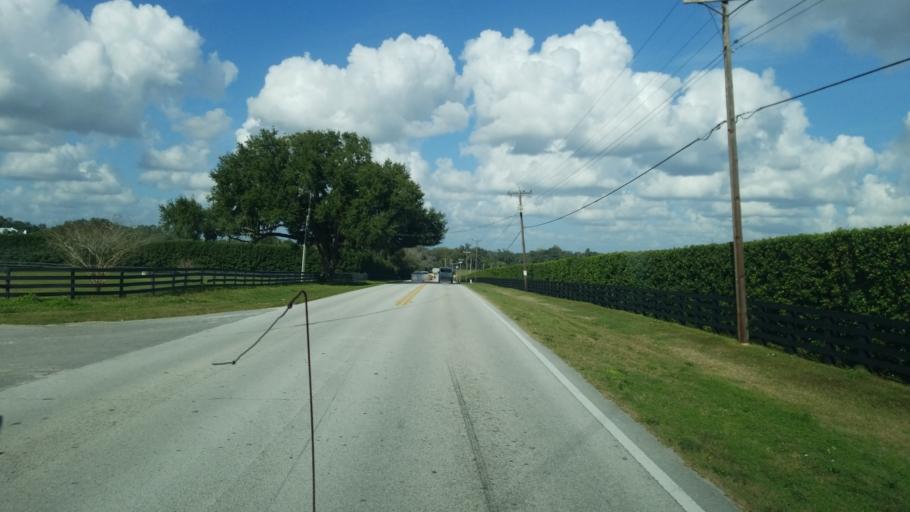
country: US
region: Florida
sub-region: Marion County
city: Ocala
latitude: 29.1285
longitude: -82.1688
